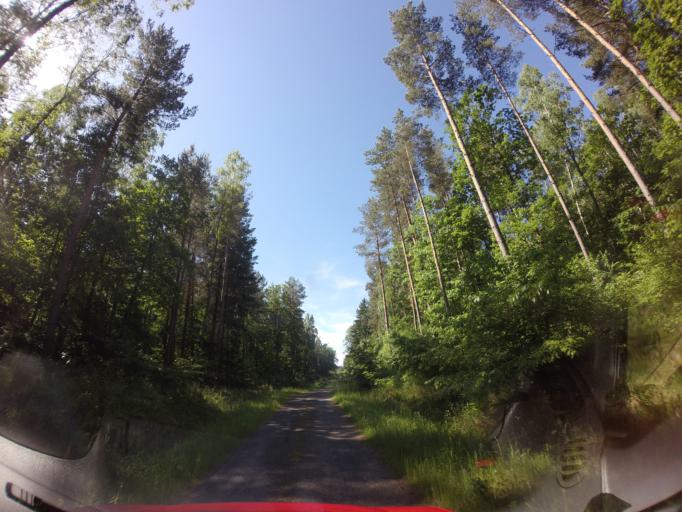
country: PL
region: West Pomeranian Voivodeship
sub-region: Powiat choszczenski
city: Choszczno
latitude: 53.1914
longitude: 15.3639
